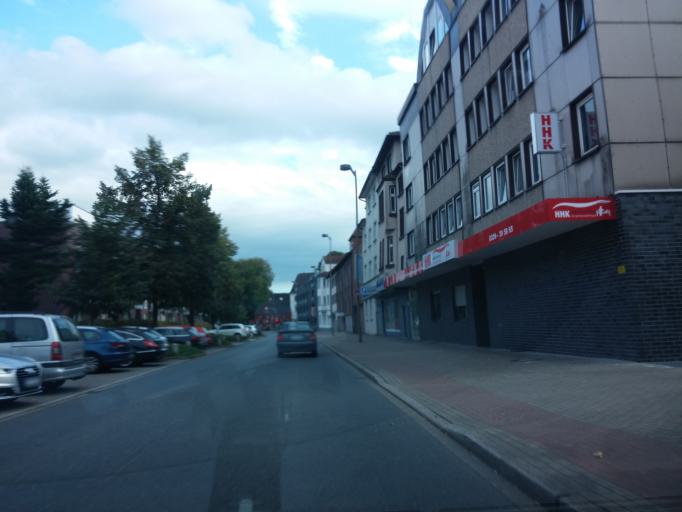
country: DE
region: North Rhine-Westphalia
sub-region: Regierungsbezirk Munster
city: Gladbeck
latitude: 51.5822
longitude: 7.0455
